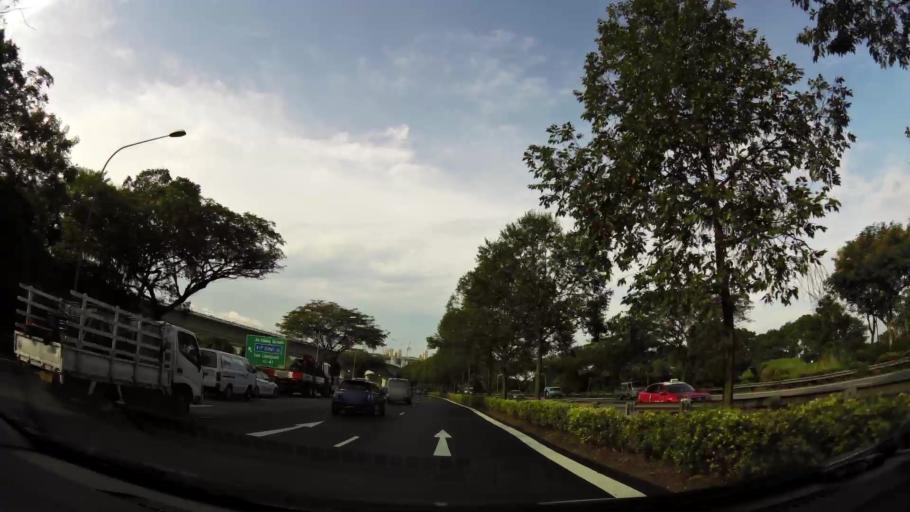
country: MY
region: Johor
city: Johor Bahru
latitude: 1.3278
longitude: 103.6676
